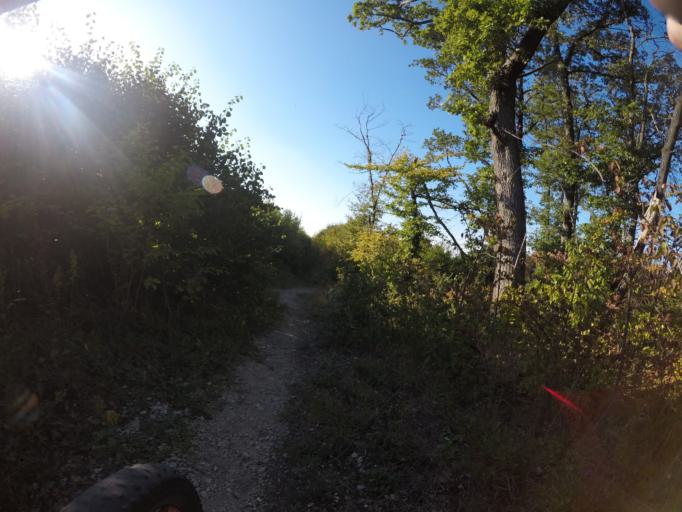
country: AT
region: Lower Austria
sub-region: Politischer Bezirk Bruck an der Leitha
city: Mannersdorf am Leithagebirge
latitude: 47.9666
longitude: 16.6151
